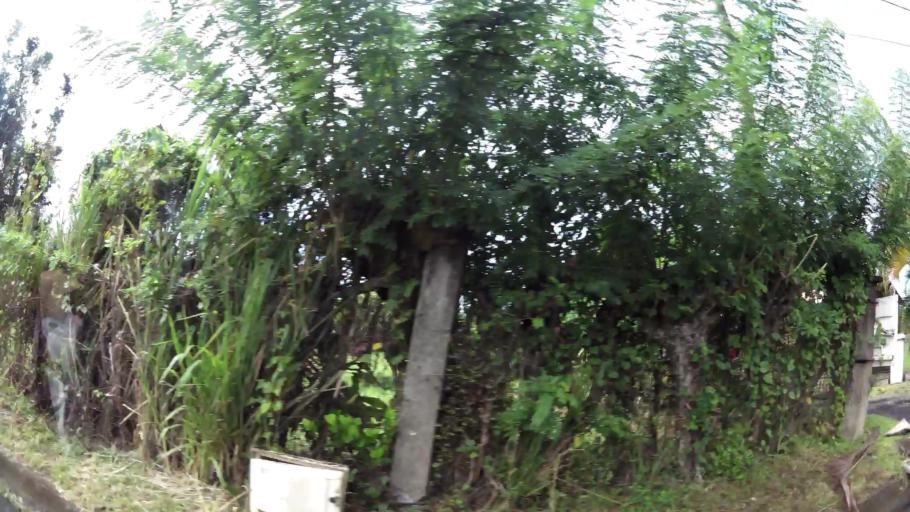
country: MQ
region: Martinique
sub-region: Martinique
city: Saint-Joseph
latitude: 14.6466
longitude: -61.0443
